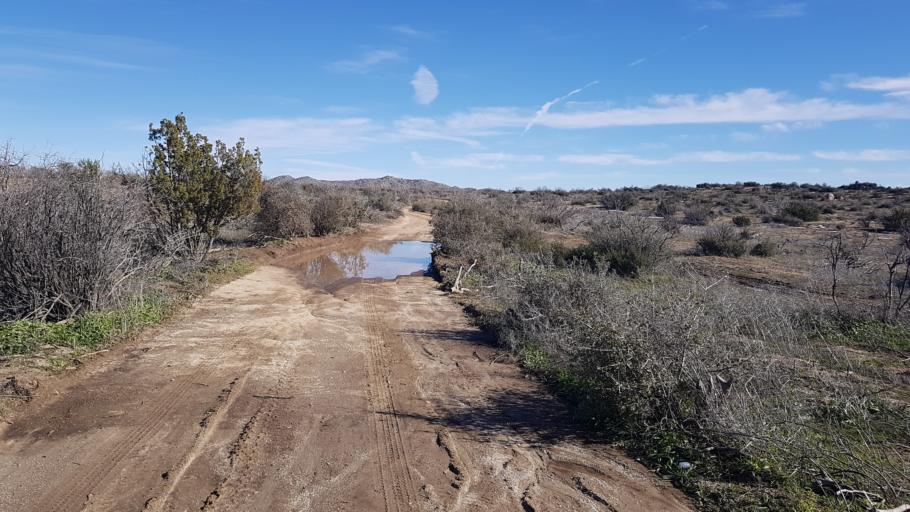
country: US
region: California
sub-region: San Diego County
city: Borrego Springs
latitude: 33.1967
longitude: -116.4948
